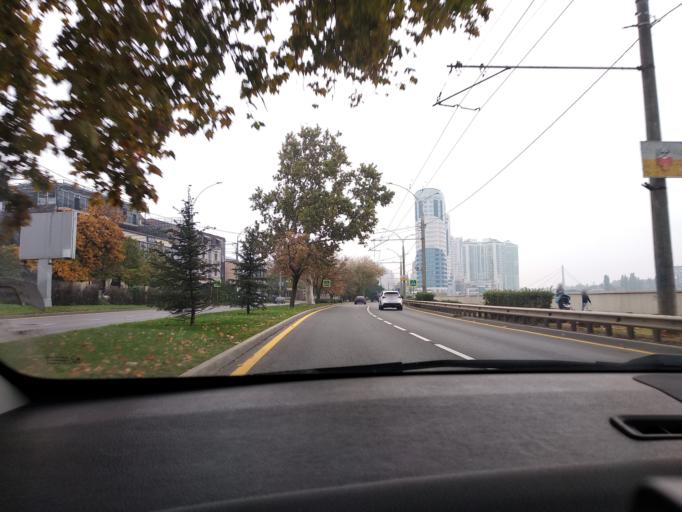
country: RU
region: Krasnodarskiy
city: Krasnodar
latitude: 45.0309
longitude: 38.9592
